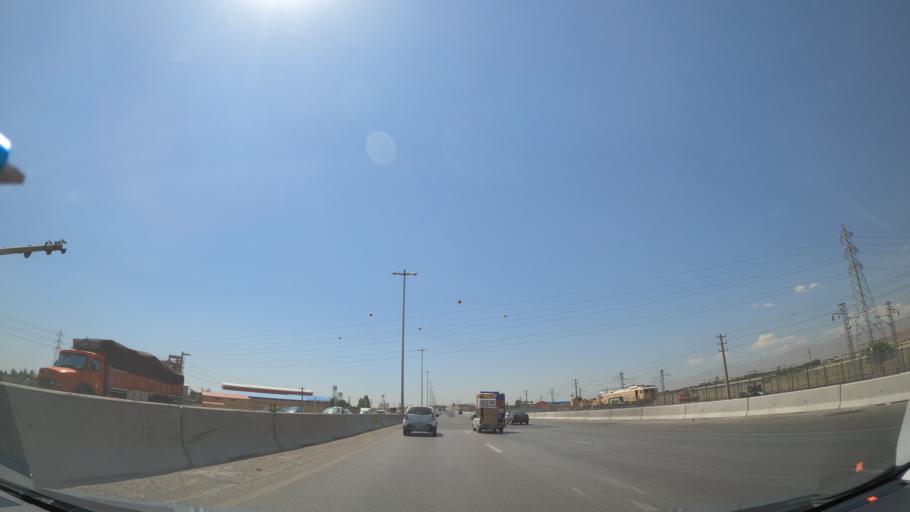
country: IR
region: Alborz
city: Karaj
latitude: 35.9066
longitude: 50.8433
